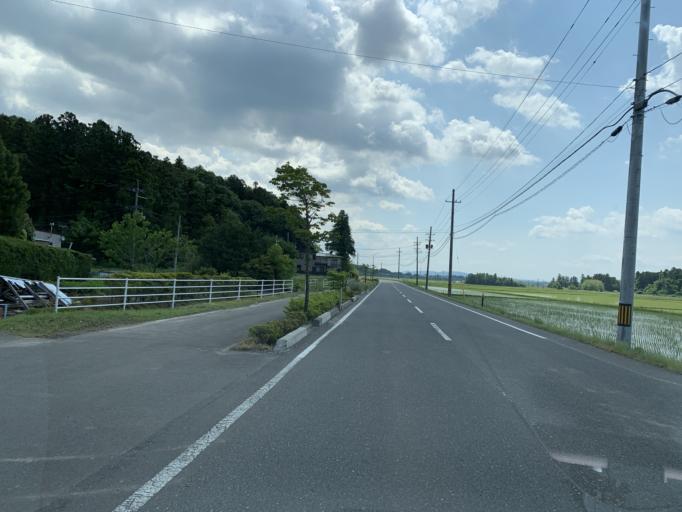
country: JP
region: Miyagi
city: Furukawa
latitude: 38.6730
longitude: 140.9864
